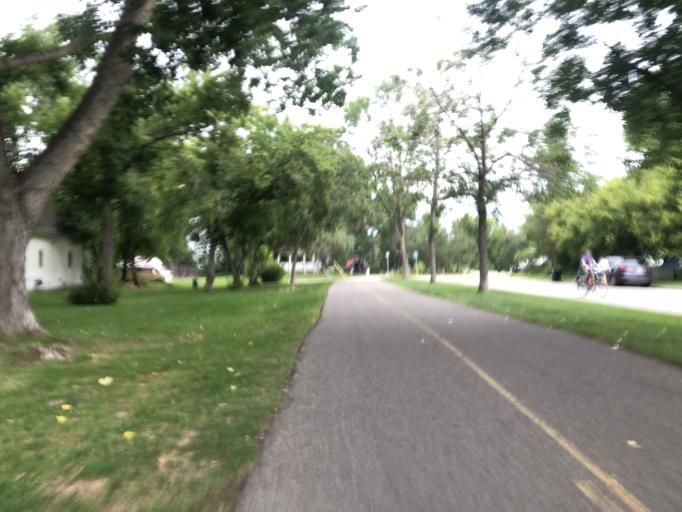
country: CA
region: Alberta
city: Calgary
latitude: 51.0409
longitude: -114.0263
